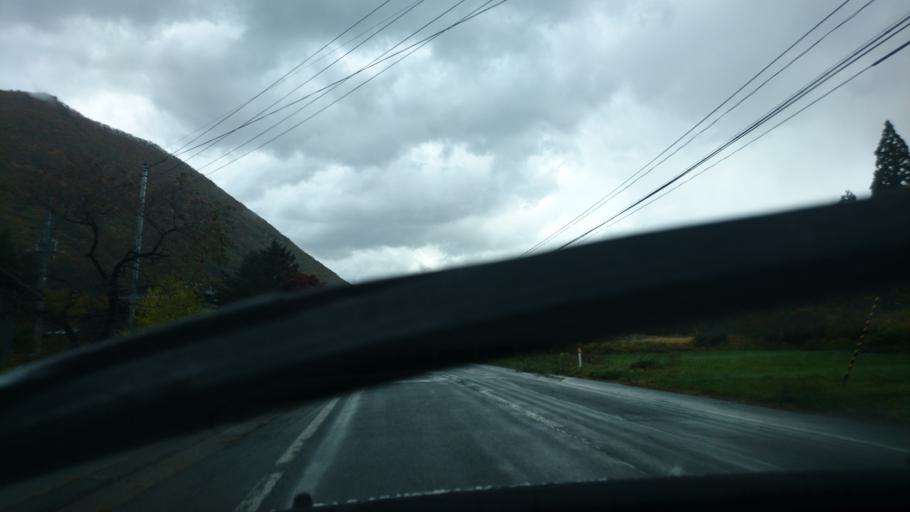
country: JP
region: Iwate
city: Shizukuishi
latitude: 39.6029
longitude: 140.9296
